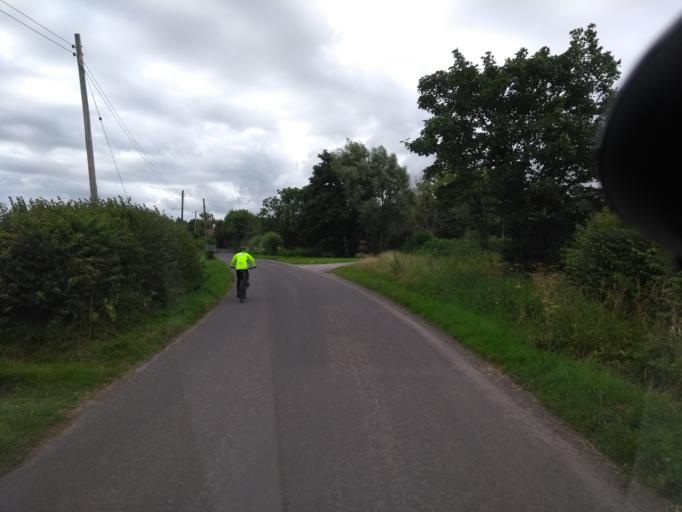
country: GB
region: England
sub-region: Somerset
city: Bishops Lydeard
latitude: 51.1873
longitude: -3.1550
